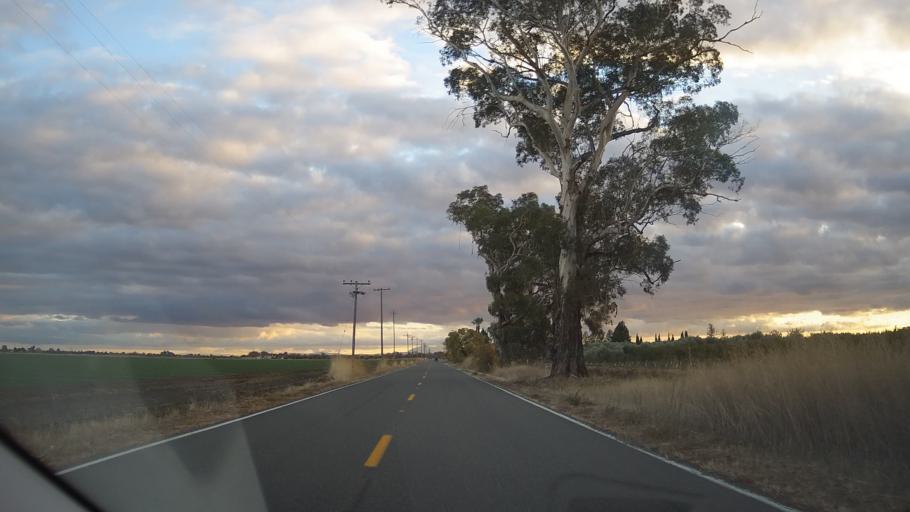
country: US
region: California
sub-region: Solano County
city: Hartley
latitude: 38.3795
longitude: -121.9059
